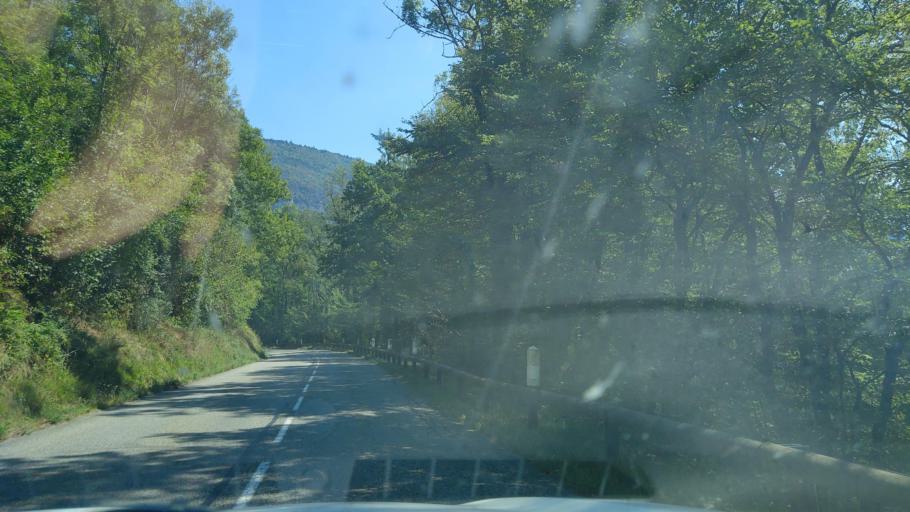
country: FR
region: Rhone-Alpes
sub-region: Departement de la Savoie
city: Novalaise
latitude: 45.5864
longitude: 5.7862
